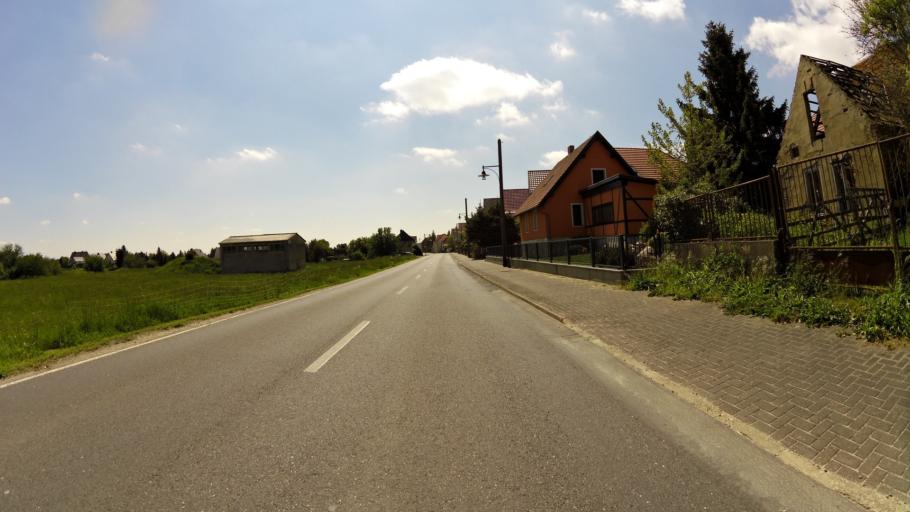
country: DE
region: Brandenburg
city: Muhlberg
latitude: 51.4473
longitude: 13.1716
